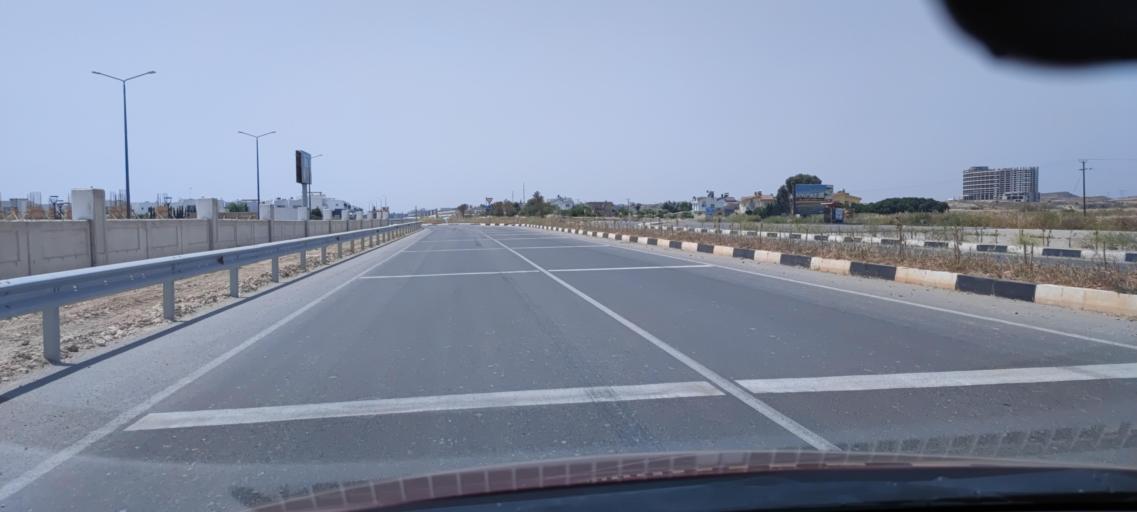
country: CY
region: Ammochostos
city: Trikomo
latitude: 35.3297
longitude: 33.9723
